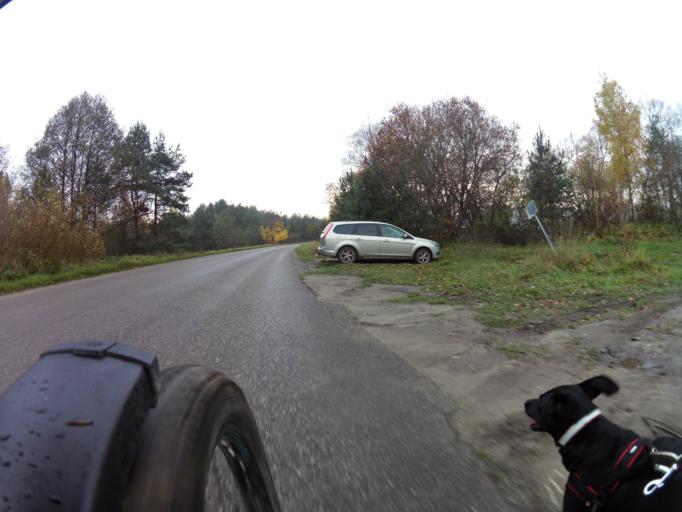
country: PL
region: Pomeranian Voivodeship
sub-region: Powiat wejherowski
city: Gniewino
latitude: 54.7353
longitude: 18.0929
